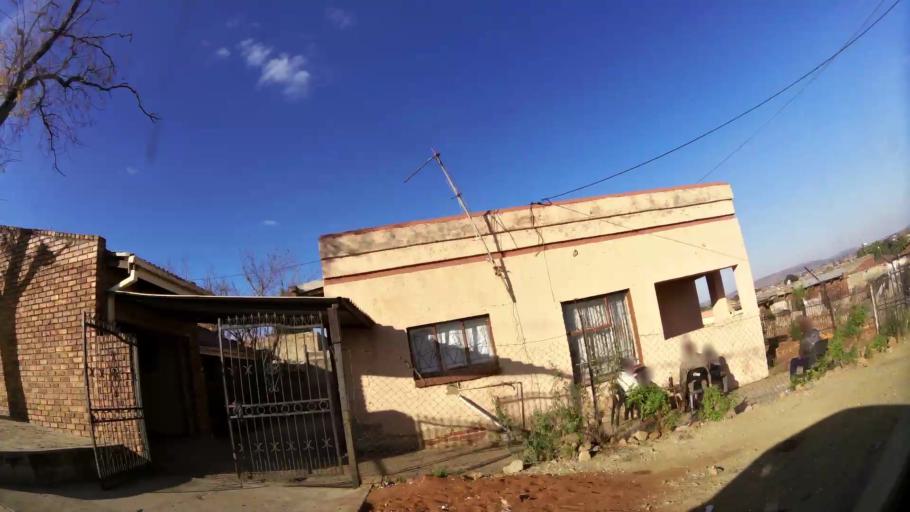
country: ZA
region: Gauteng
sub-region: City of Tshwane Metropolitan Municipality
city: Cullinan
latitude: -25.7036
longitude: 28.3832
